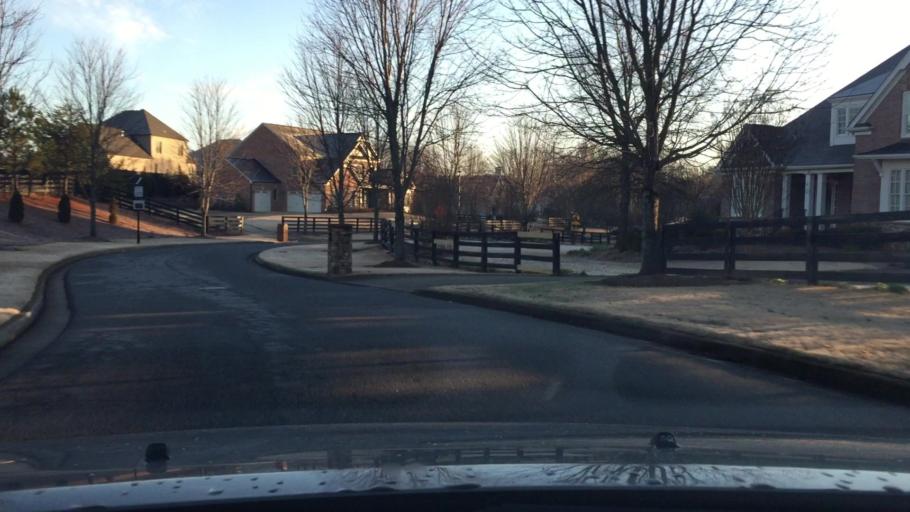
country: US
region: Georgia
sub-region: Forsyth County
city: Cumming
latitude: 34.1883
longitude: -84.1995
